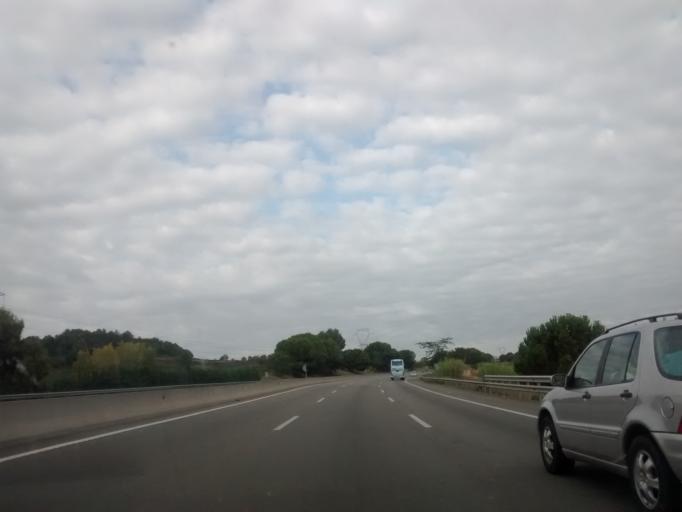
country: ES
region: Catalonia
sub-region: Provincia de Barcelona
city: La Granada
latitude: 41.3877
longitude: 1.7568
